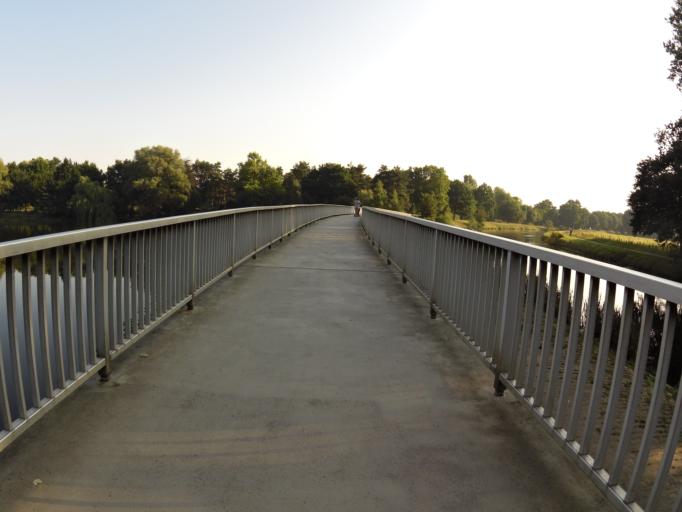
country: DE
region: North Rhine-Westphalia
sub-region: Regierungsbezirk Munster
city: Warendorf
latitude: 51.9533
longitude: 8.0058
